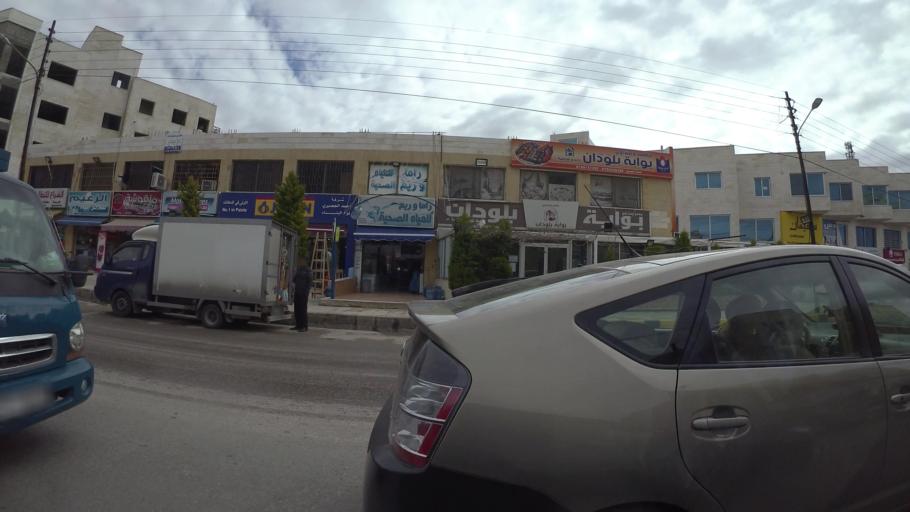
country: JO
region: Amman
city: Wadi as Sir
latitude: 31.9470
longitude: 35.8399
